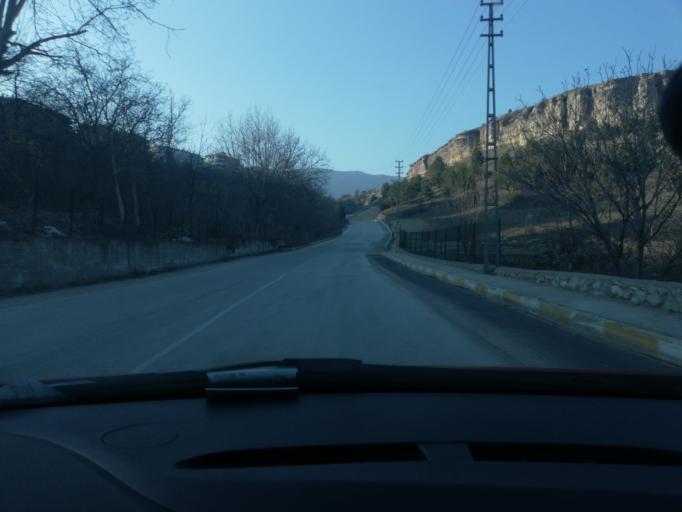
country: TR
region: Karabuk
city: Safranbolu
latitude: 41.2536
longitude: 32.6867
